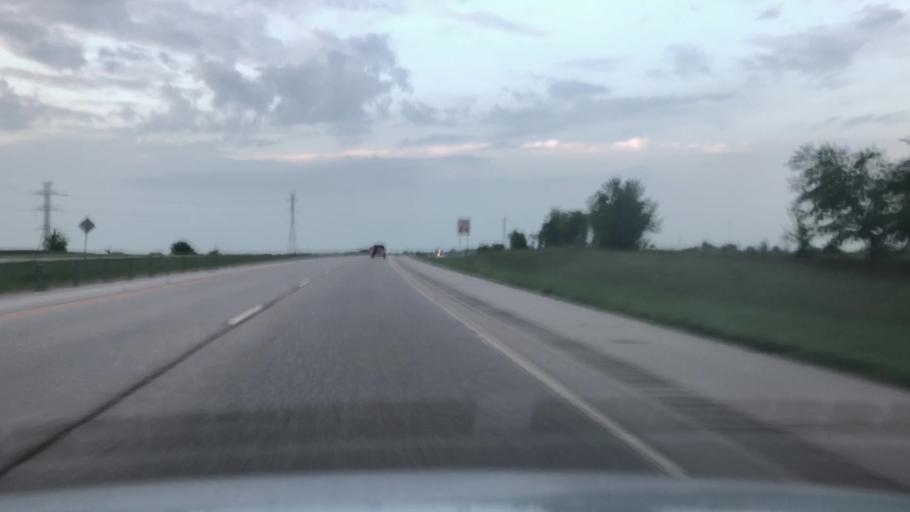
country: US
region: Oklahoma
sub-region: Tulsa County
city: Sperry
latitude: 36.3394
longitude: -95.9239
